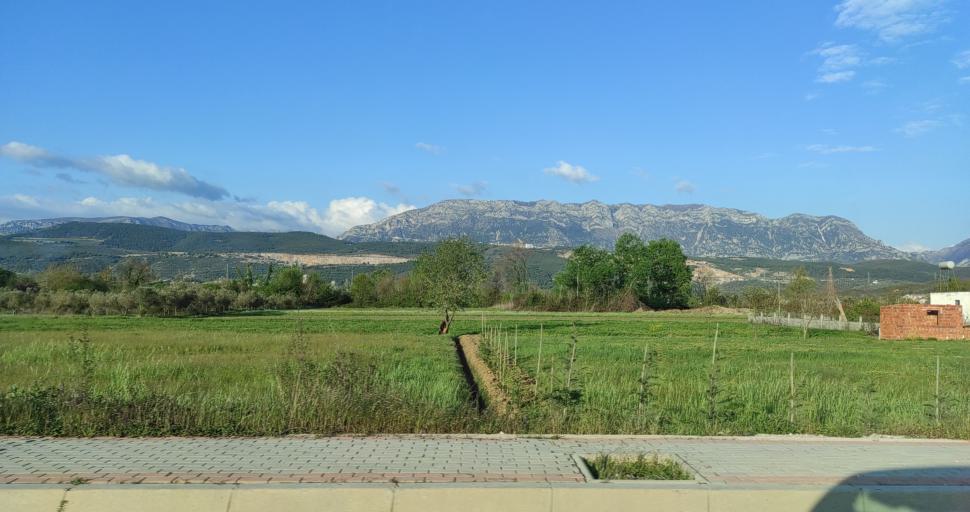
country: AL
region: Durres
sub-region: Rrethi i Krujes
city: Fushe-Kruje
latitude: 41.4893
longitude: 19.7246
